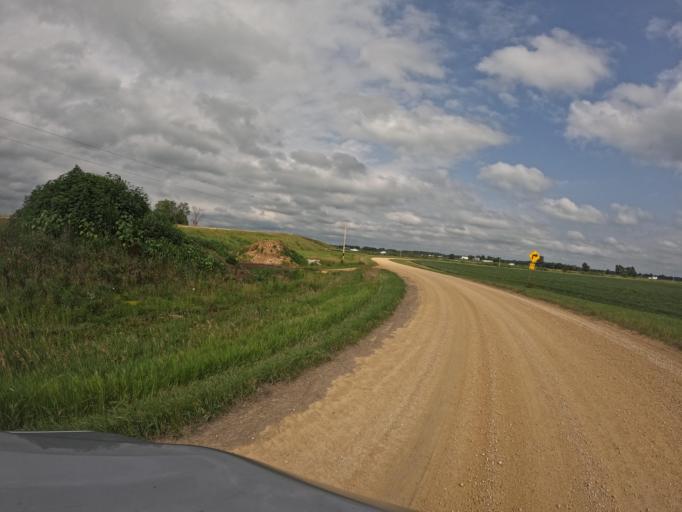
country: US
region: Iowa
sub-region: Clinton County
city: De Witt
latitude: 41.7851
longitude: -90.5703
